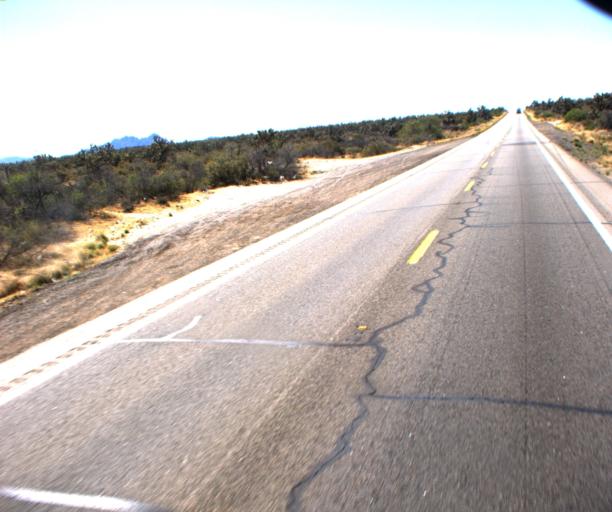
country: US
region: Arizona
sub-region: Yavapai County
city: Congress
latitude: 34.2611
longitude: -113.0884
